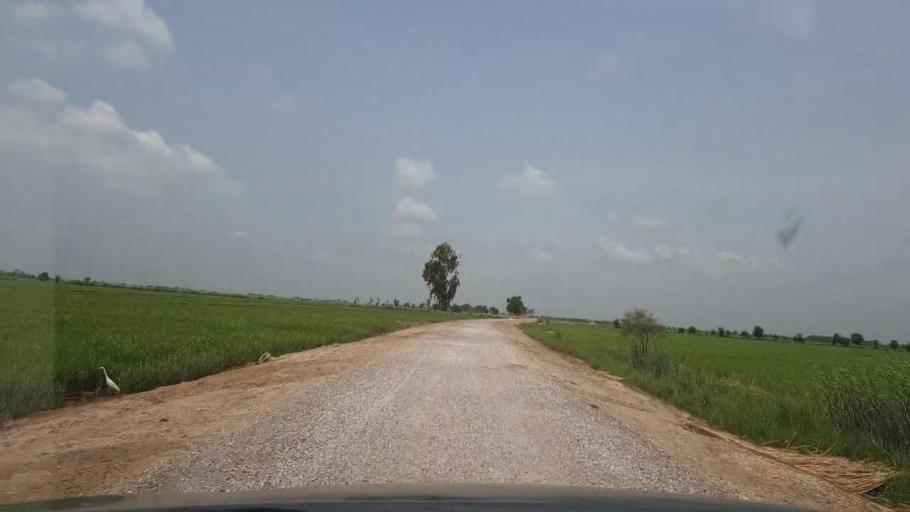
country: PK
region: Sindh
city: Ratodero
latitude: 27.9138
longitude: 68.3170
